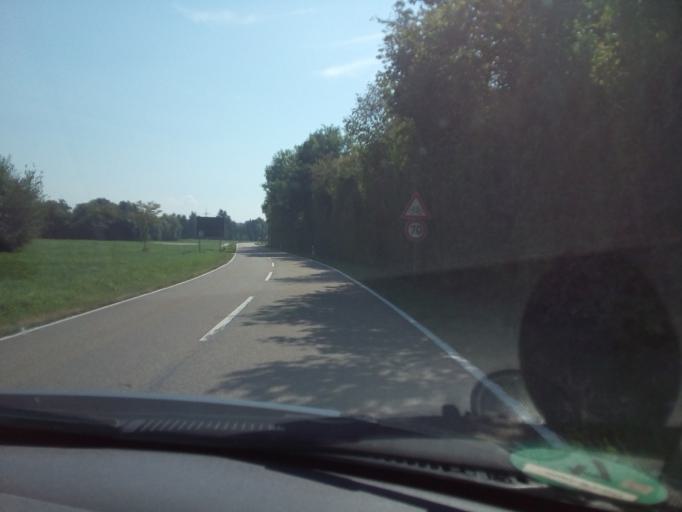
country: DE
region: Baden-Wuerttemberg
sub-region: Karlsruhe Region
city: Zell
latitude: 48.7281
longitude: 8.0857
